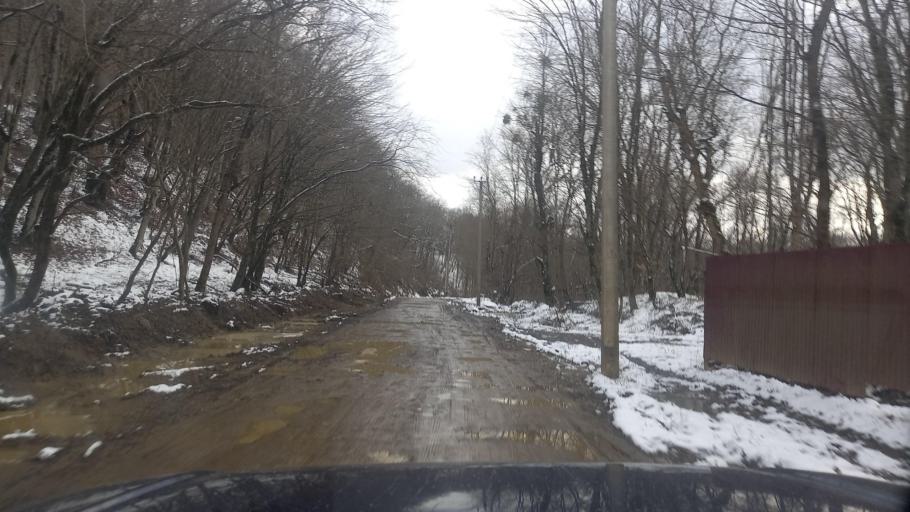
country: RU
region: Krasnodarskiy
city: Smolenskaya
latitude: 44.7014
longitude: 38.8268
